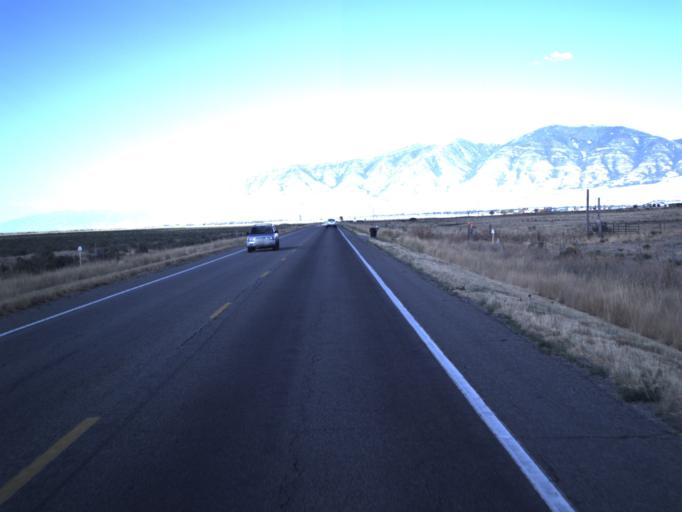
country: US
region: Utah
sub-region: Tooele County
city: Erda
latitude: 40.6125
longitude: -112.3748
